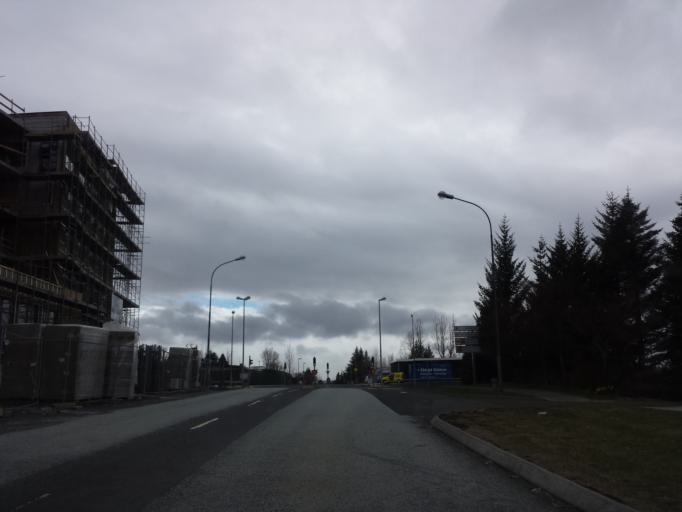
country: IS
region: Capital Region
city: Gardabaer
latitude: 64.0892
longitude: -21.9220
